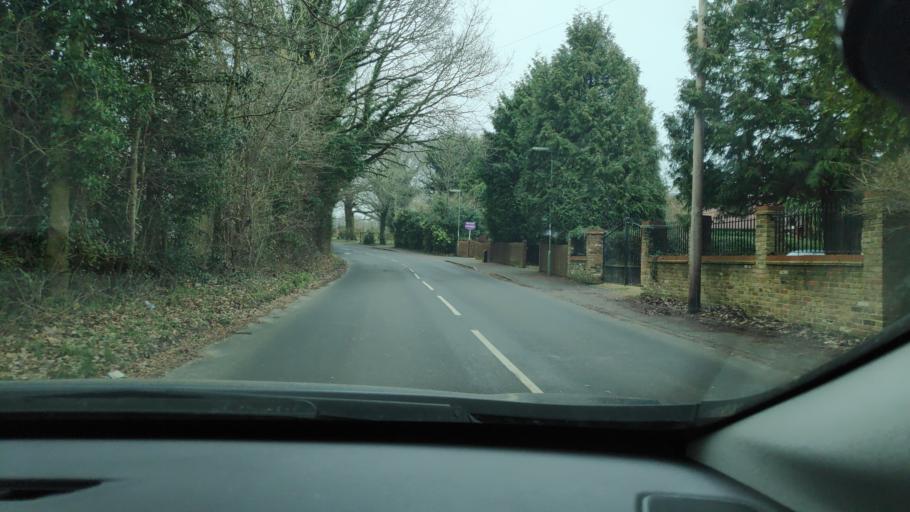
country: GB
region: England
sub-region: Surrey
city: Seale
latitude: 51.2460
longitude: -0.7143
